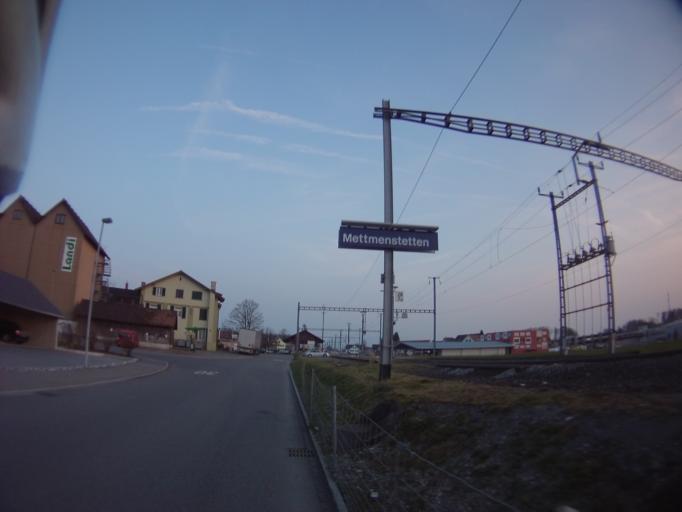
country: CH
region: Zurich
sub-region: Bezirk Affoltern
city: Mettmenstetten
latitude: 47.2459
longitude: 8.4568
